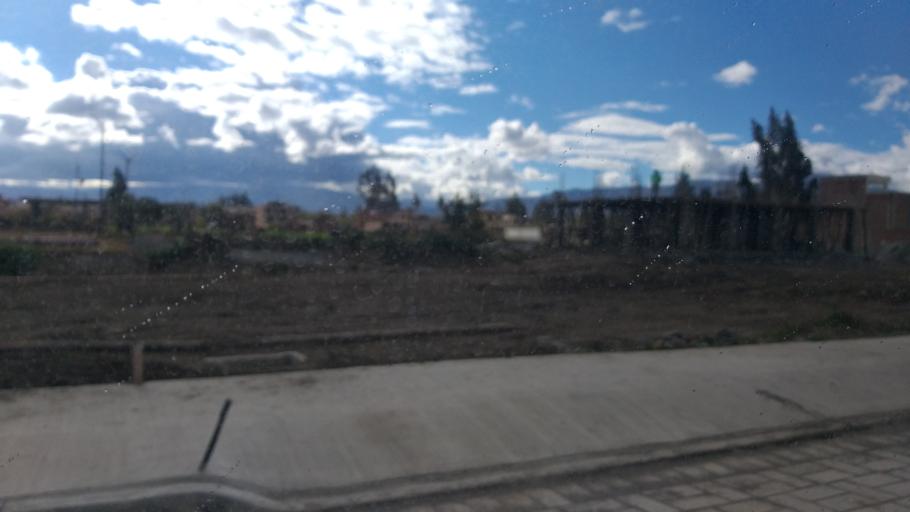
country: EC
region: Chimborazo
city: Riobamba
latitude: -1.6873
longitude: -78.6241
